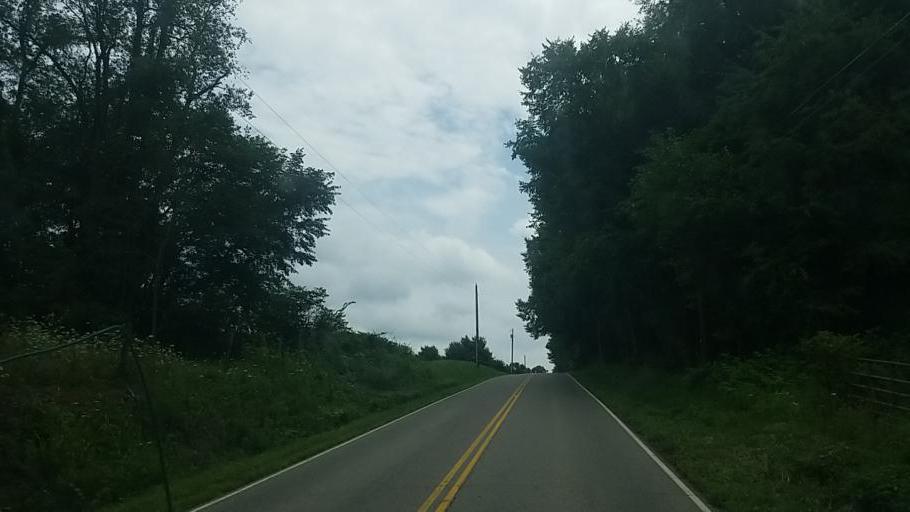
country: US
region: Ohio
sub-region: Licking County
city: Utica
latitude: 40.2215
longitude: -82.3660
